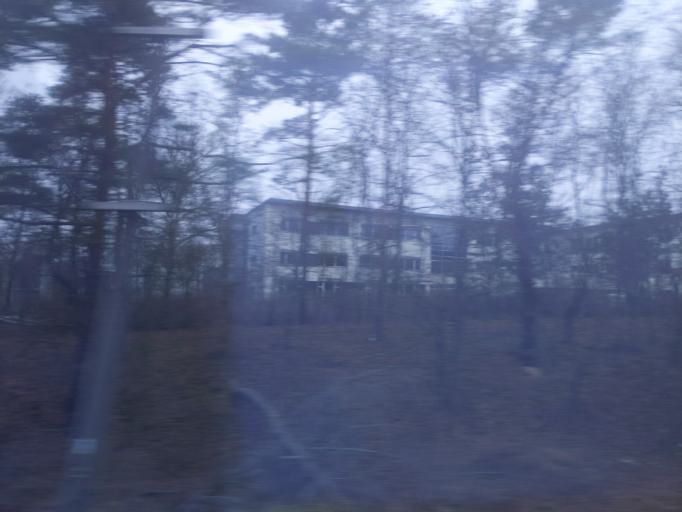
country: DE
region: Saxony
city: Albertstadt
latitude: 51.0949
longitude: 13.7697
